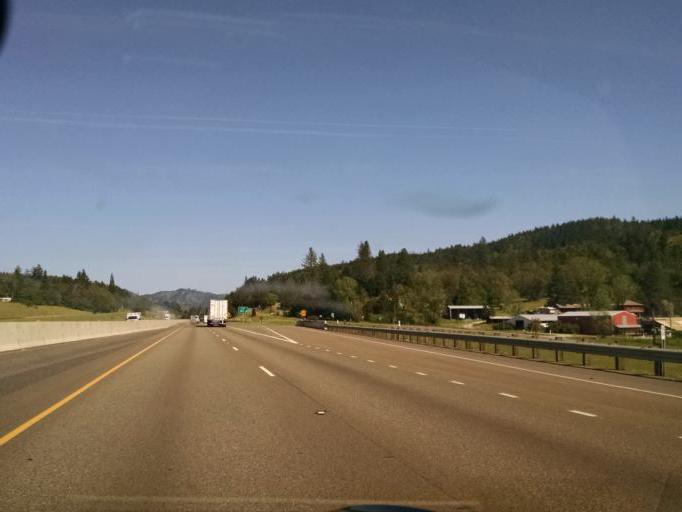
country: US
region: Oregon
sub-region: Douglas County
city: Tri-City
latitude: 42.9479
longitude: -123.3212
